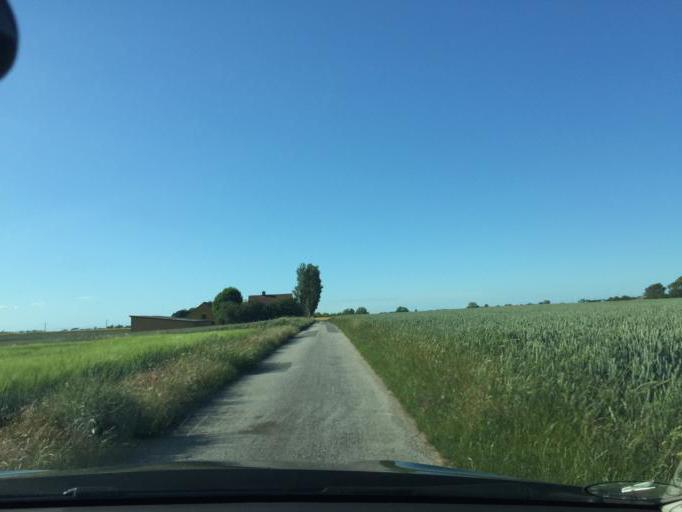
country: DK
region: Zealand
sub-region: Slagelse Kommune
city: Skaelskor
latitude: 55.2014
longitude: 11.1816
